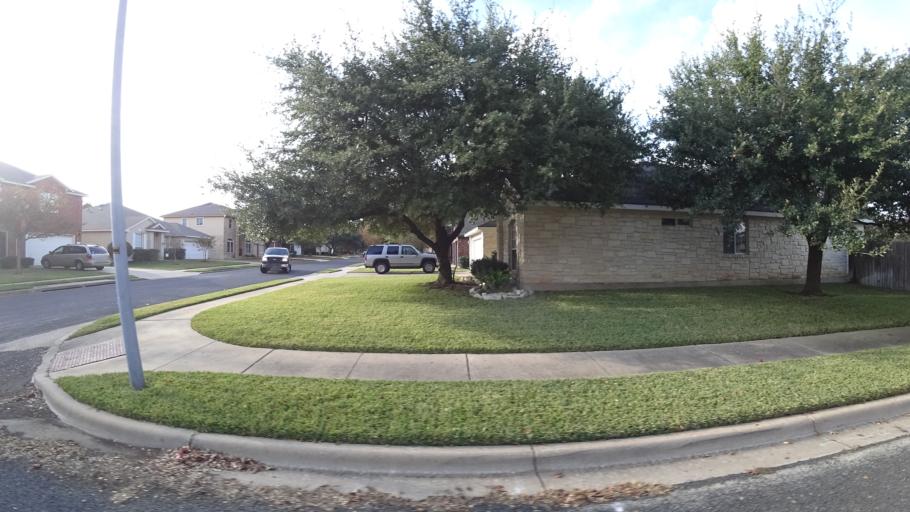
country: US
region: Texas
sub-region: Williamson County
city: Brushy Creek
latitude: 30.5030
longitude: -97.7267
